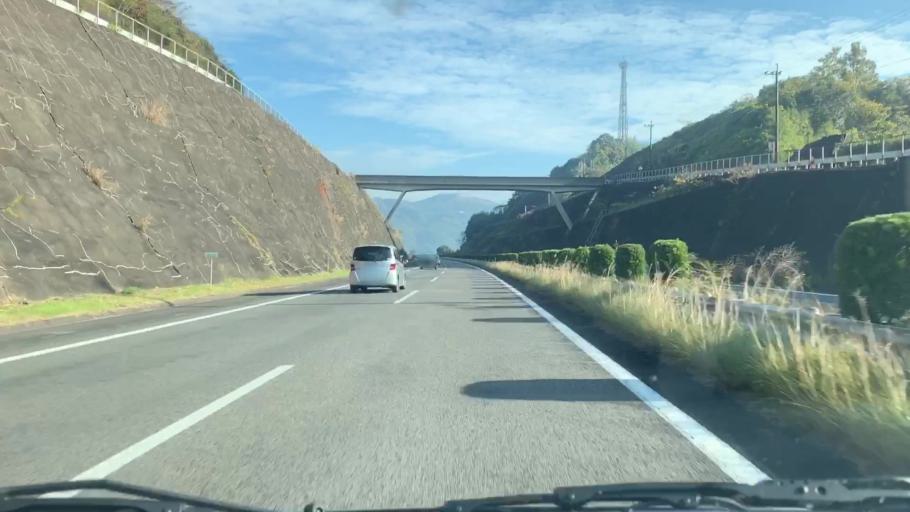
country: JP
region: Saga Prefecture
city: Takeocho-takeo
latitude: 33.2778
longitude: 130.1167
